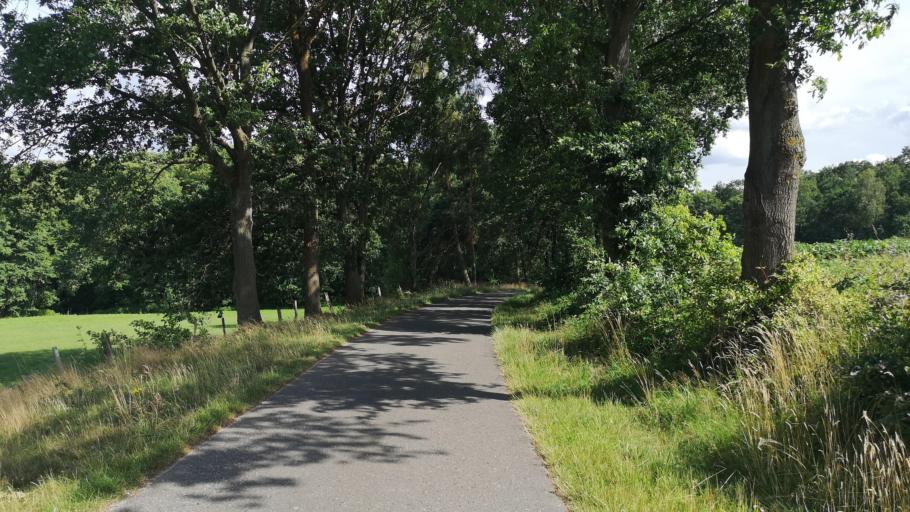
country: DE
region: Lower Saxony
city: Thomasburg
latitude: 53.2255
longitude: 10.6618
